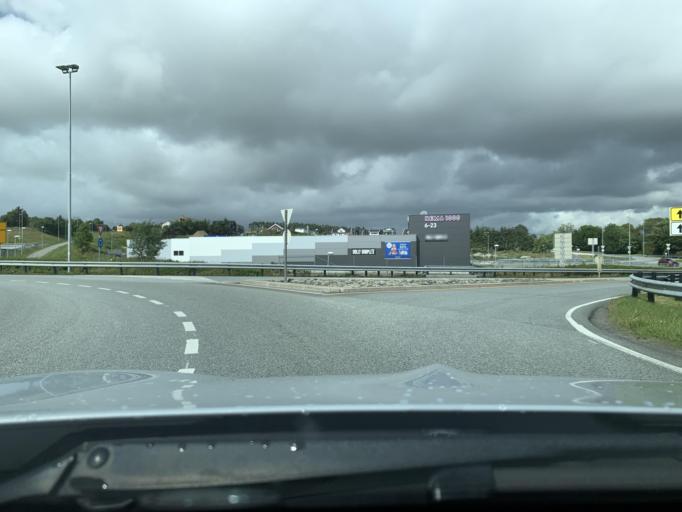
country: NO
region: Rogaland
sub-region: Sandnes
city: Sandnes
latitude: 58.8125
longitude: 5.6972
